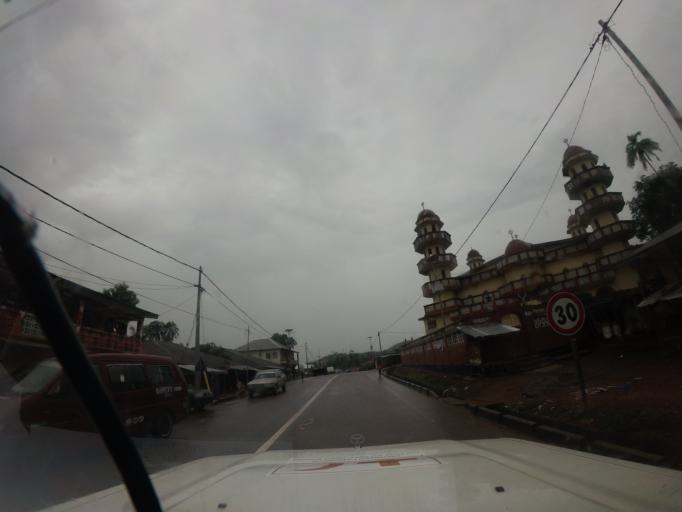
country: SL
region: Northern Province
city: Makeni
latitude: 8.8874
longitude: -12.0448
